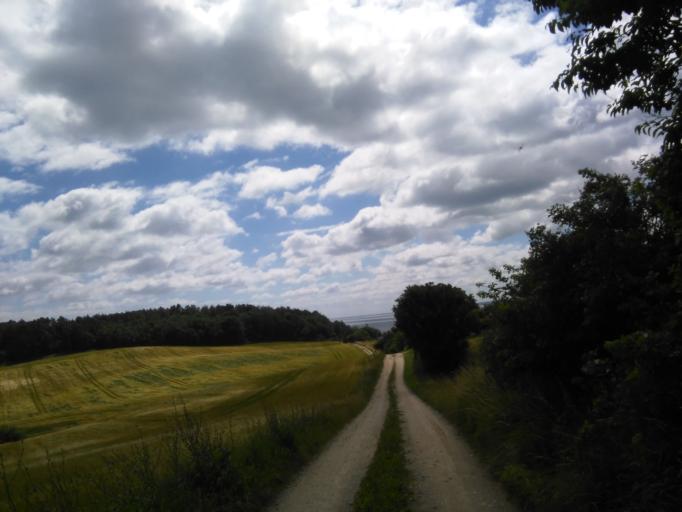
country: DK
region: Central Jutland
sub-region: Arhus Kommune
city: Logten
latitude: 56.1671
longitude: 10.3987
